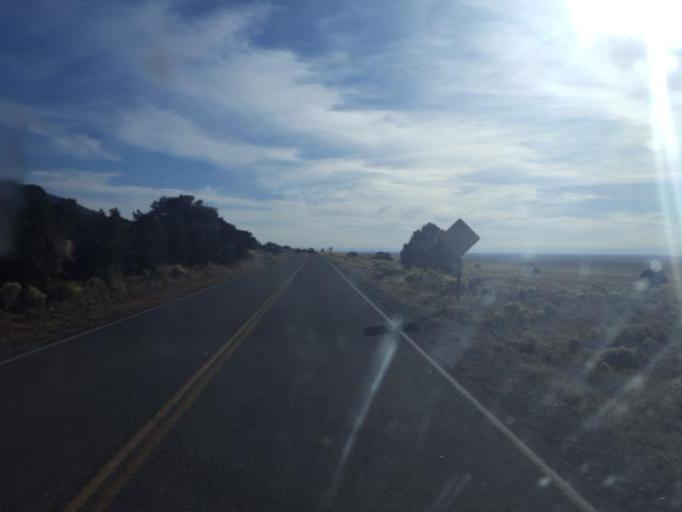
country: US
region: Colorado
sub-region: Alamosa County
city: Alamosa East
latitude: 37.7273
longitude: -105.5177
